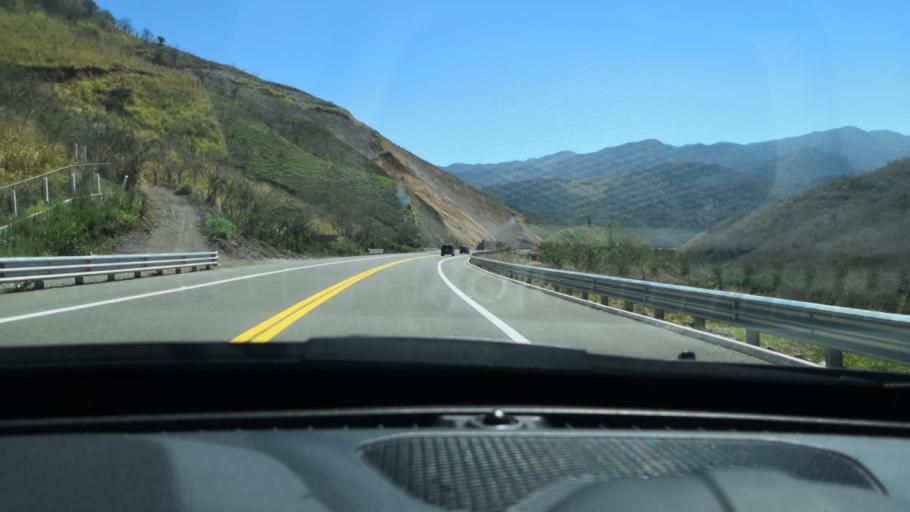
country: MX
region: Nayarit
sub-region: Compostela
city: Juan Escutia (Borbollon)
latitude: 21.1506
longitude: -104.9092
